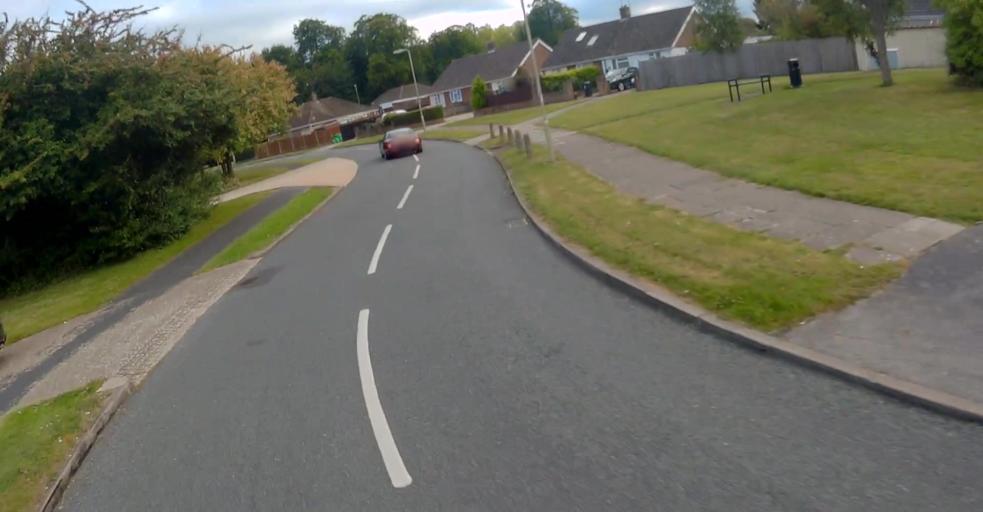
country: GB
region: England
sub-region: Hampshire
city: Basingstoke
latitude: 51.2507
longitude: -1.1189
